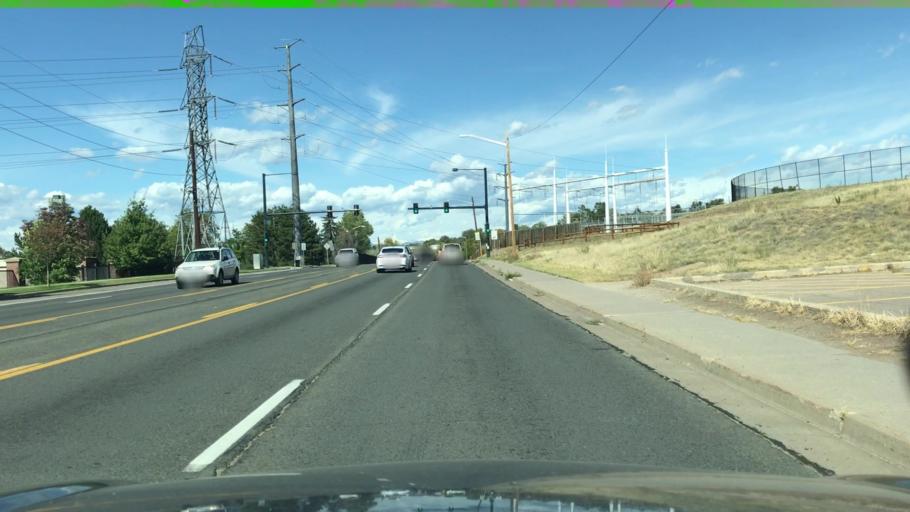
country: US
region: Colorado
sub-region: Arapahoe County
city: Glendale
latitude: 39.7048
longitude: -104.9165
